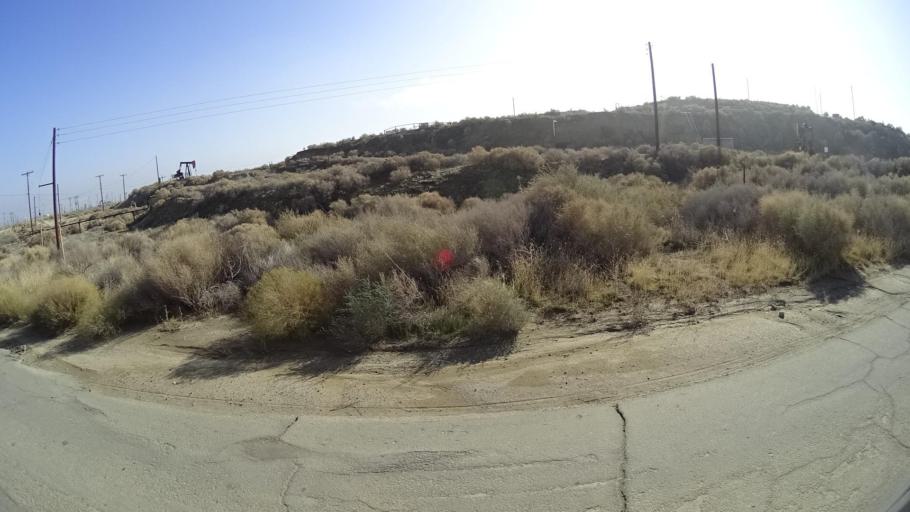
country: US
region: California
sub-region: Kern County
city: Taft Heights
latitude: 35.2209
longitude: -119.5983
